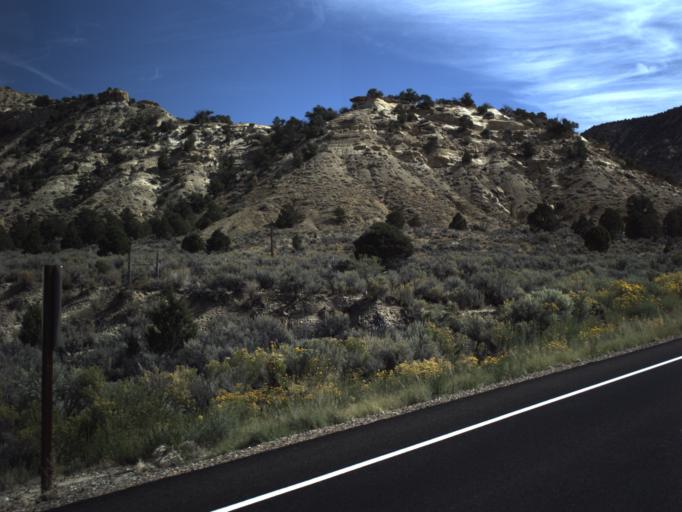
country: US
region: Utah
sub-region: Garfield County
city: Panguitch
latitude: 37.5925
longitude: -111.9329
